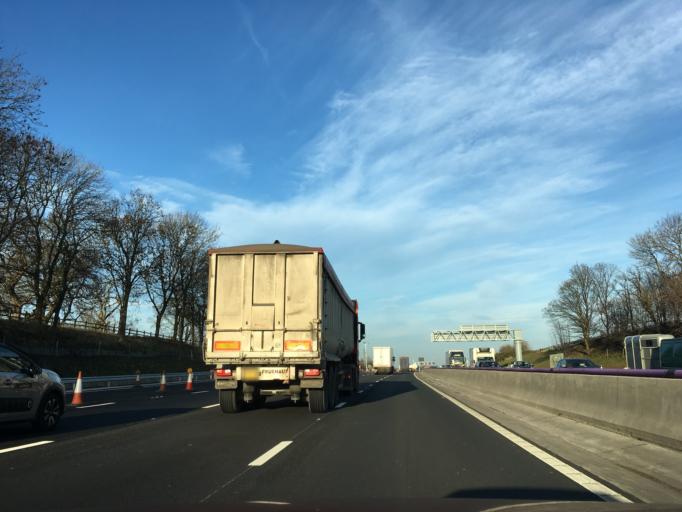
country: GB
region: England
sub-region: Cheshire East
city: Sandbach
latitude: 53.1558
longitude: -2.3491
